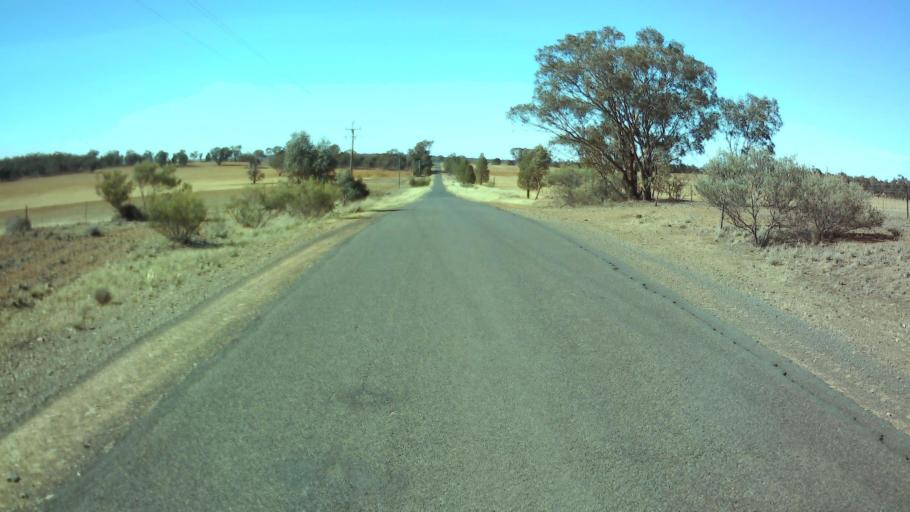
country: AU
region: New South Wales
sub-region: Weddin
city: Grenfell
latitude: -33.7628
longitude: 147.8291
